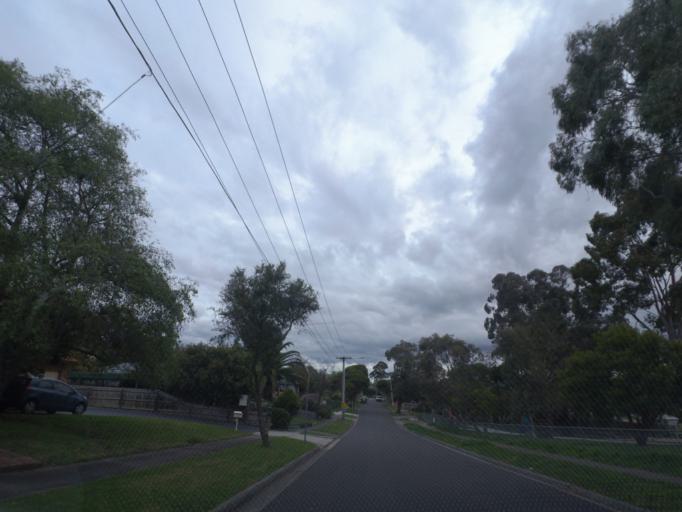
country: AU
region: Victoria
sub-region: Maroondah
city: Croydon North
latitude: -37.7718
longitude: 145.3107
